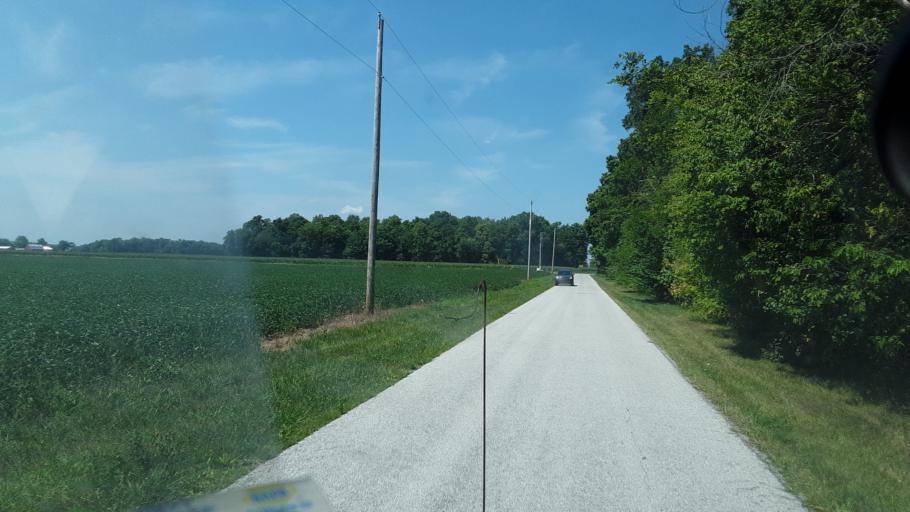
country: US
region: Ohio
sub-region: Hancock County
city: Findlay
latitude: 40.9923
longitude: -83.5332
